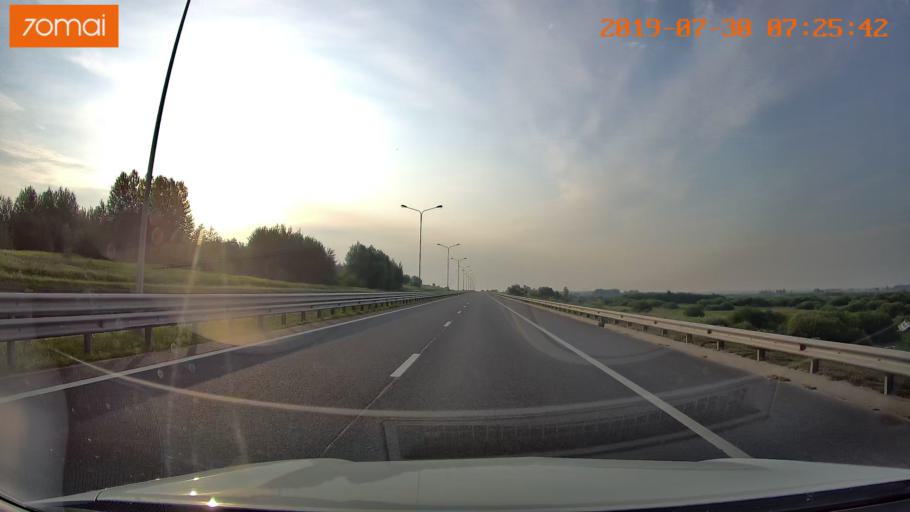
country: RU
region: Kaliningrad
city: Gvardeysk
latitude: 54.6855
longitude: 20.8407
